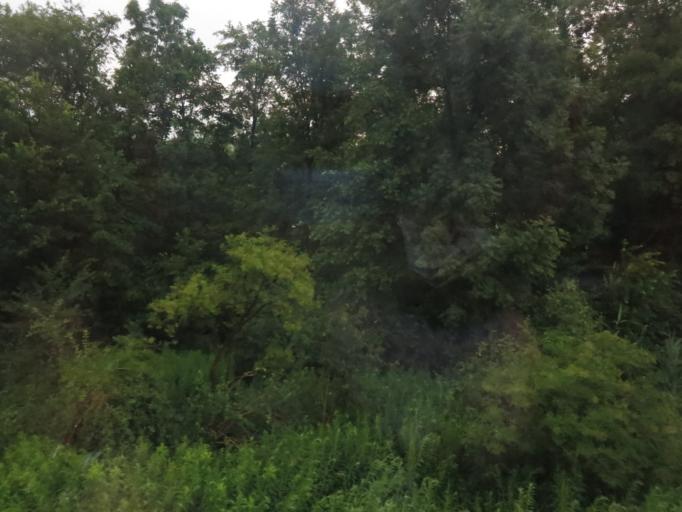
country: CH
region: Schwyz
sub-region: Bezirk March
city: Lachen
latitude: 47.1915
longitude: 8.8707
